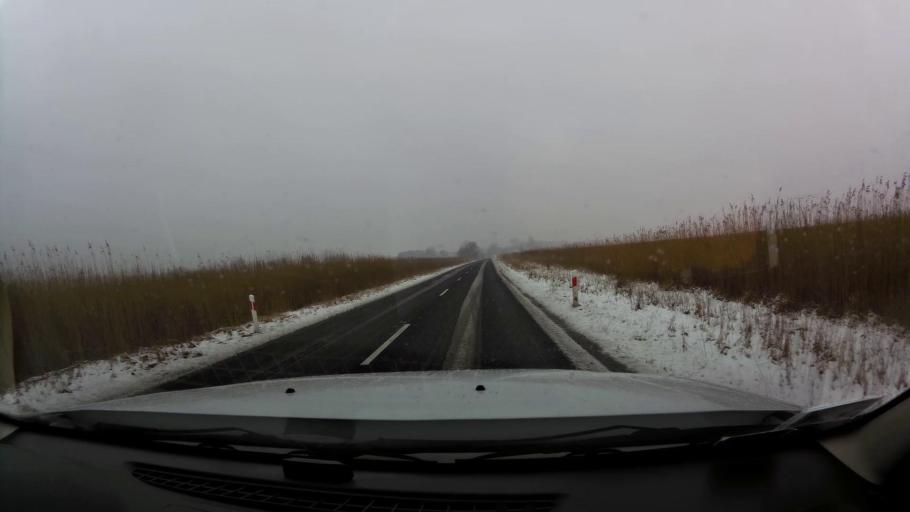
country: PL
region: West Pomeranian Voivodeship
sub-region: Powiat gryficki
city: Mrzezyno
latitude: 54.1305
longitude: 15.2785
